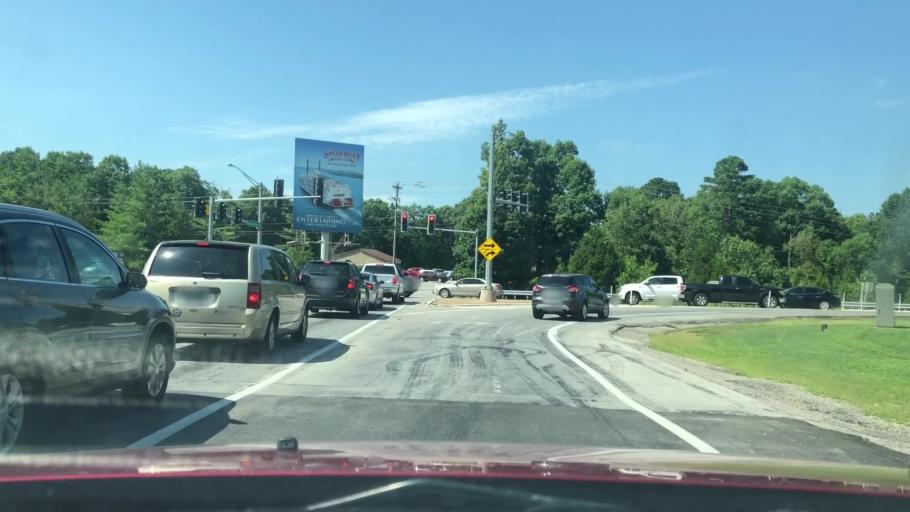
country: US
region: Missouri
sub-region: Stone County
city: Kimberling City
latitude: 36.6708
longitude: -93.3351
